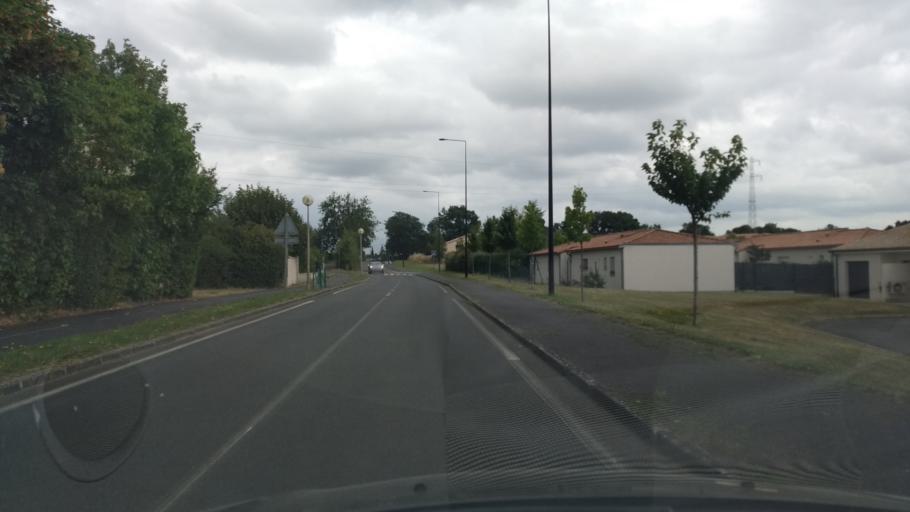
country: FR
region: Poitou-Charentes
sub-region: Departement de la Vienne
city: Smarves
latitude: 46.5100
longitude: 0.3543
